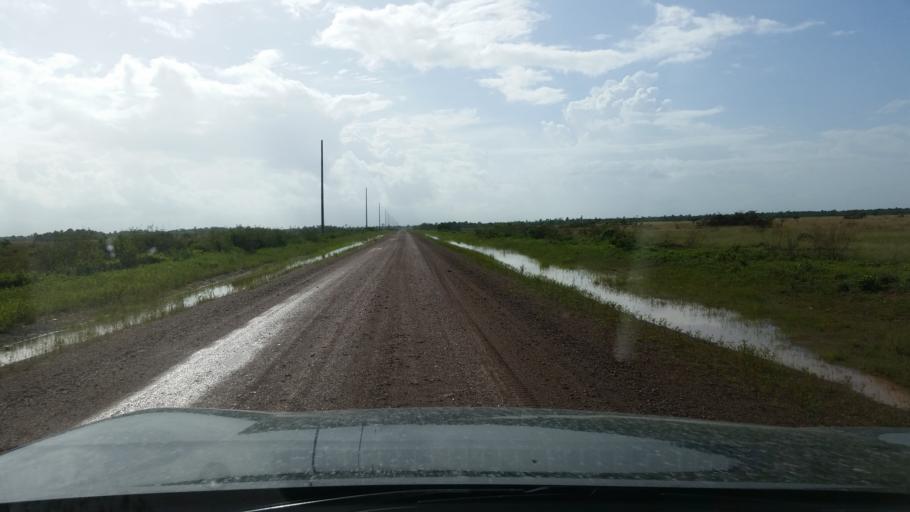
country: NI
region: Atlantico Norte (RAAN)
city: Puerto Cabezas
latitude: 14.1096
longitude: -83.5922
